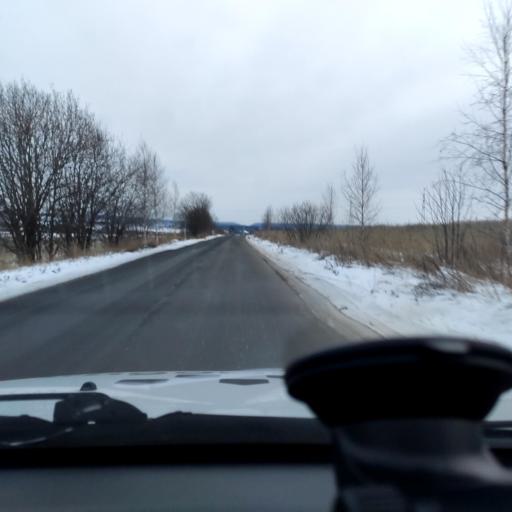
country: RU
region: Perm
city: Ferma
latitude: 57.9337
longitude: 56.3263
